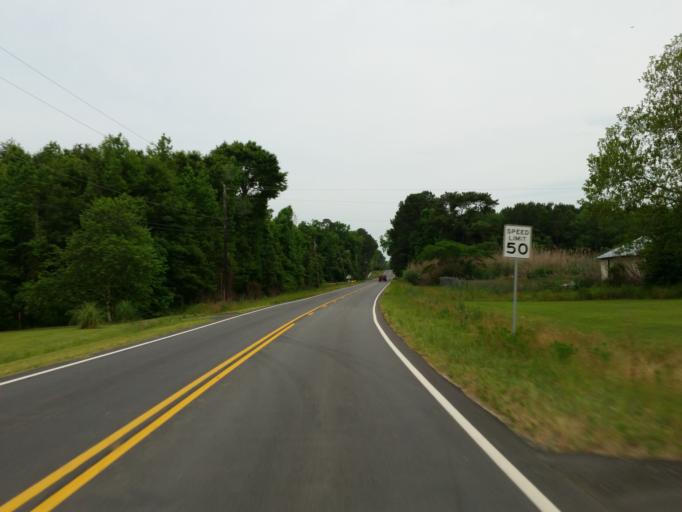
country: US
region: Georgia
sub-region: Dooly County
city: Unadilla
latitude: 32.2754
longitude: -83.7400
